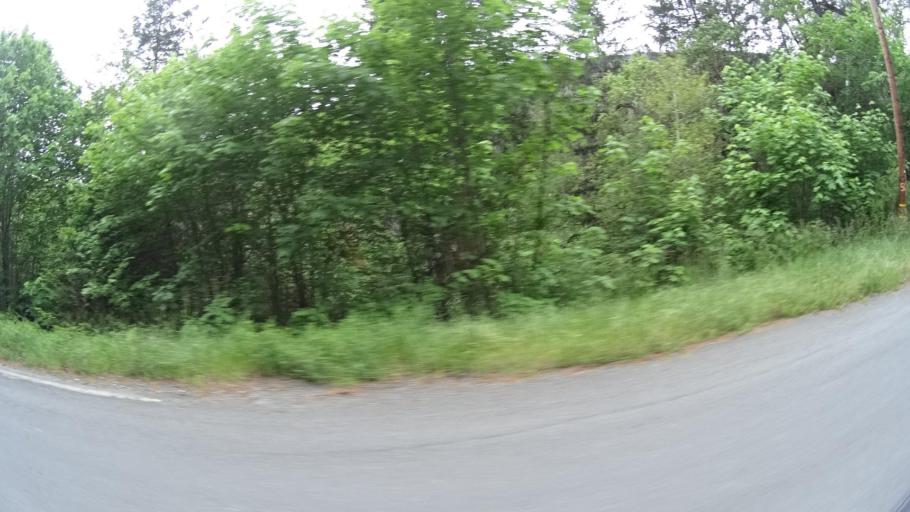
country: US
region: California
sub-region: Humboldt County
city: Willow Creek
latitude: 41.2056
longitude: -123.7535
